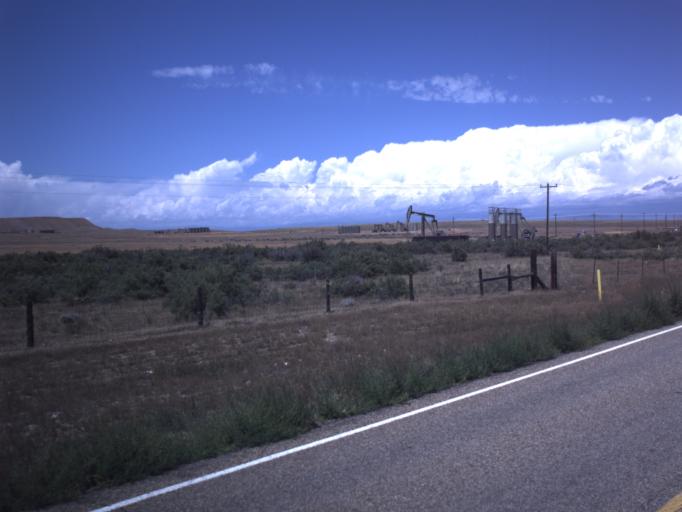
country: US
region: Utah
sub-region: Uintah County
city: Naples
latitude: 40.1150
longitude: -109.6678
